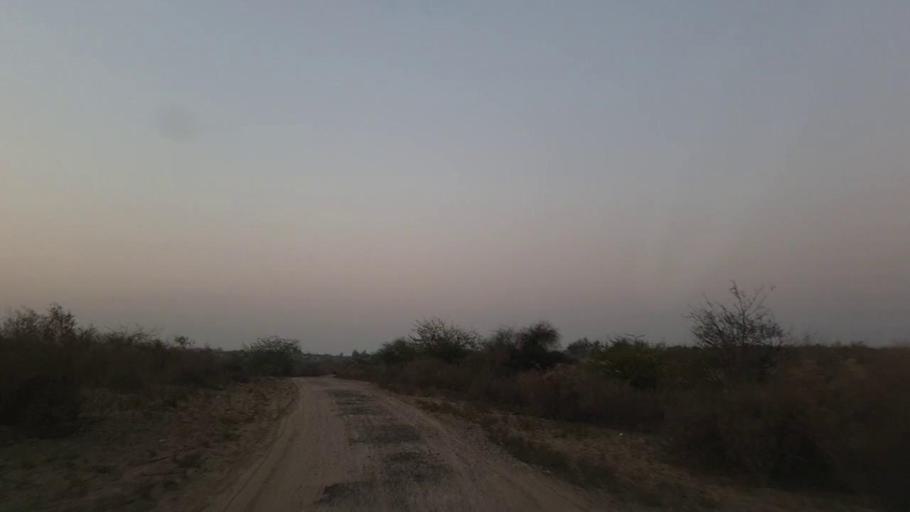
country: PK
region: Sindh
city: Bandhi
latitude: 26.6104
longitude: 68.3899
